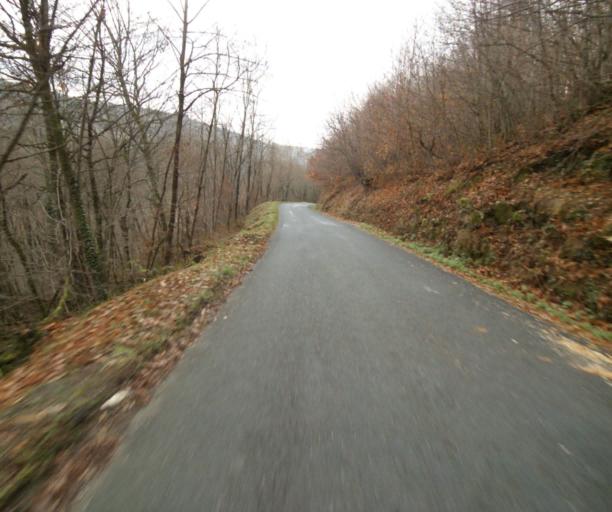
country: FR
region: Limousin
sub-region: Departement de la Correze
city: Chameyrat
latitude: 45.2258
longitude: 1.7040
